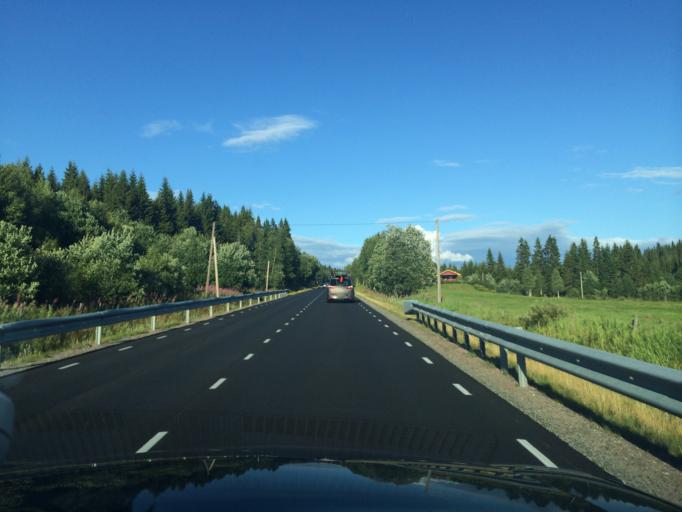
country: NO
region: Hedmark
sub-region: Elverum
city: Elverum
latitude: 61.0472
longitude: 11.8880
